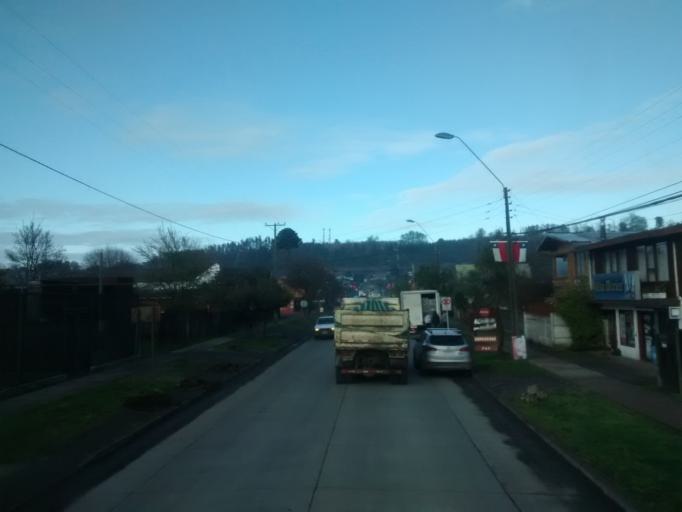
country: CL
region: Araucania
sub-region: Provincia de Cautin
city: Villarrica
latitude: -39.2777
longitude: -72.2317
